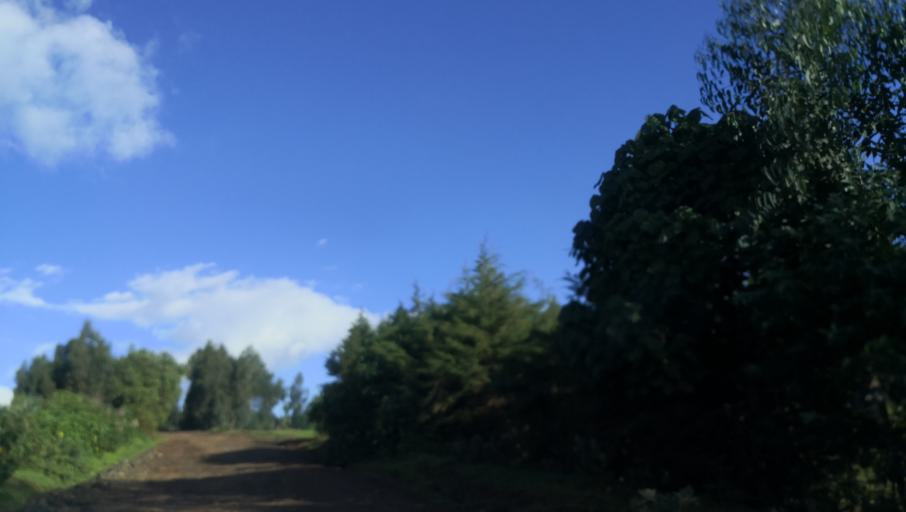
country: ET
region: Southern Nations, Nationalities, and People's Region
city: Butajira
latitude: 8.3936
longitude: 38.3083
